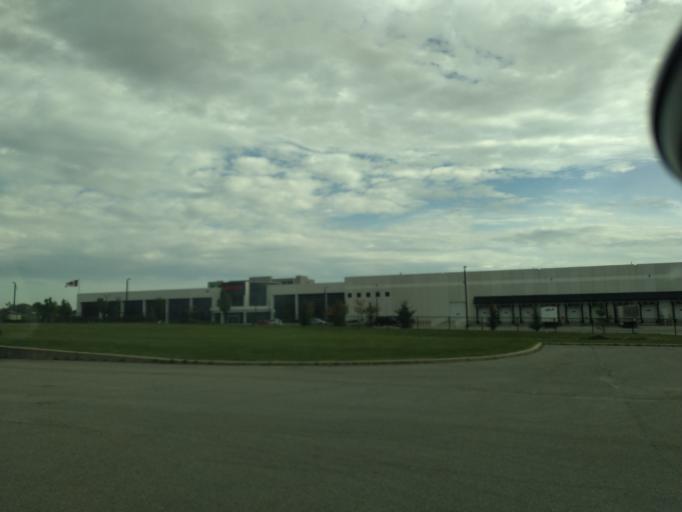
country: CA
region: Ontario
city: Newmarket
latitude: 44.0096
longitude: -79.4096
